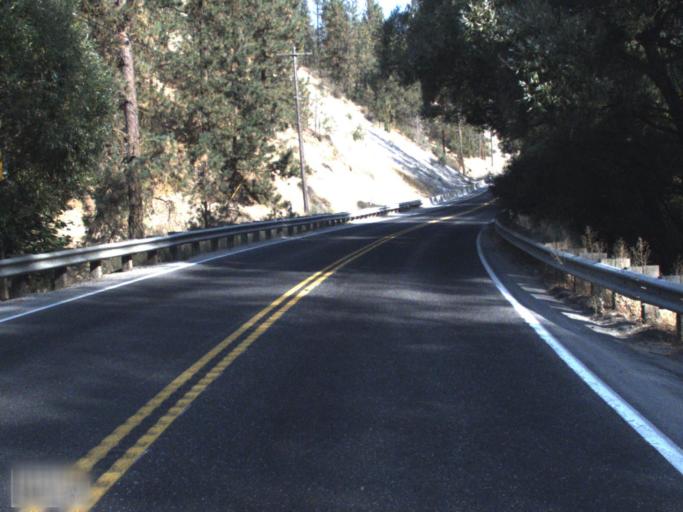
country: US
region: Washington
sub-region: Spokane County
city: Fairwood
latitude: 47.8051
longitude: -117.5543
